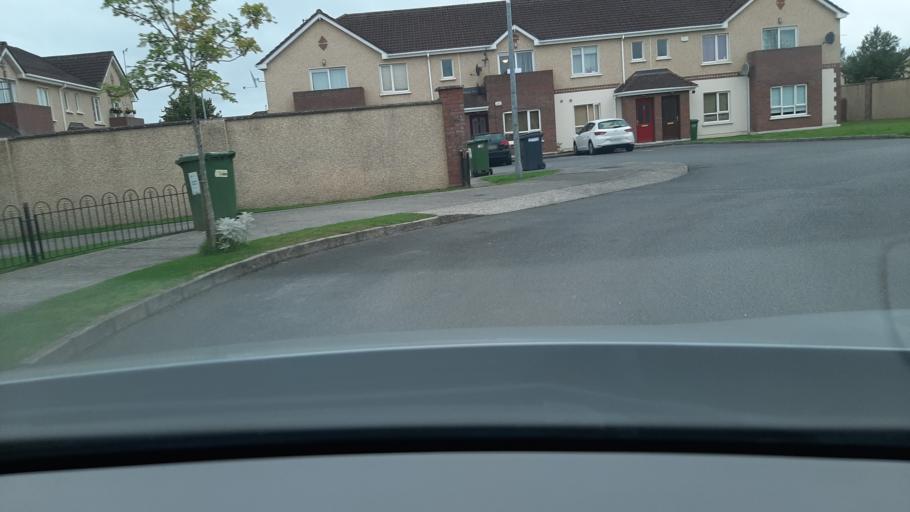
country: IE
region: Leinster
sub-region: Kildare
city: Kildare
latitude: 53.1574
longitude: -6.8955
